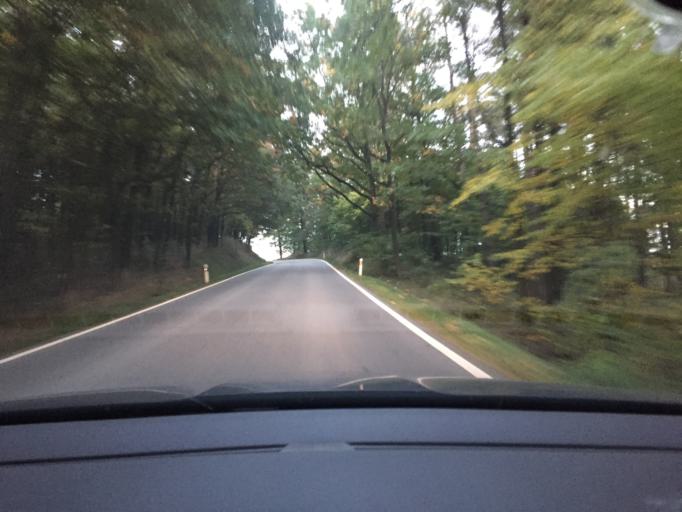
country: CZ
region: Jihocesky
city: Hrdejovice
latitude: 49.0555
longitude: 14.4775
